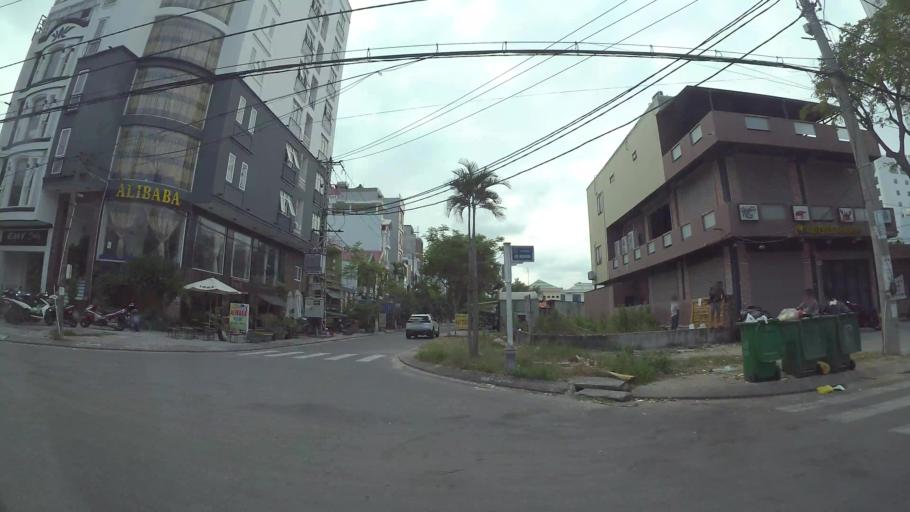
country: VN
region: Da Nang
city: Son Tra
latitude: 16.0722
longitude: 108.2430
